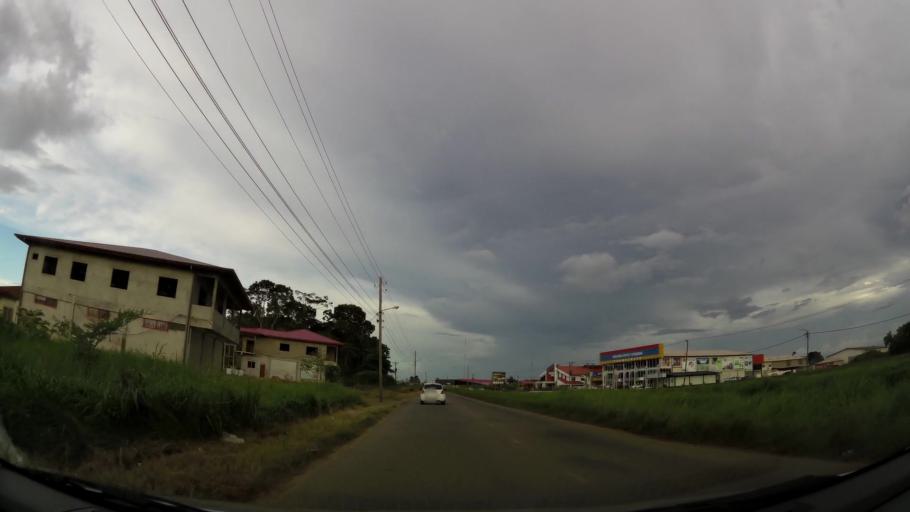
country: SR
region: Paramaribo
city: Paramaribo
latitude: 5.8575
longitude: -55.1734
